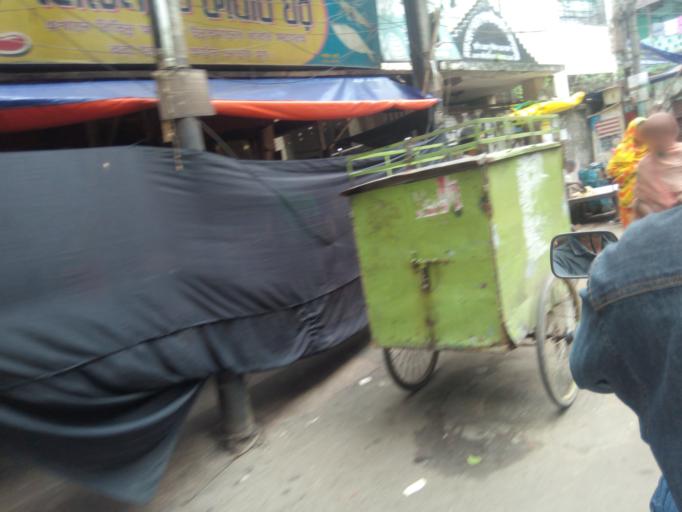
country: BD
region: Dhaka
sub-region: Dhaka
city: Dhaka
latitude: 23.7118
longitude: 90.4132
